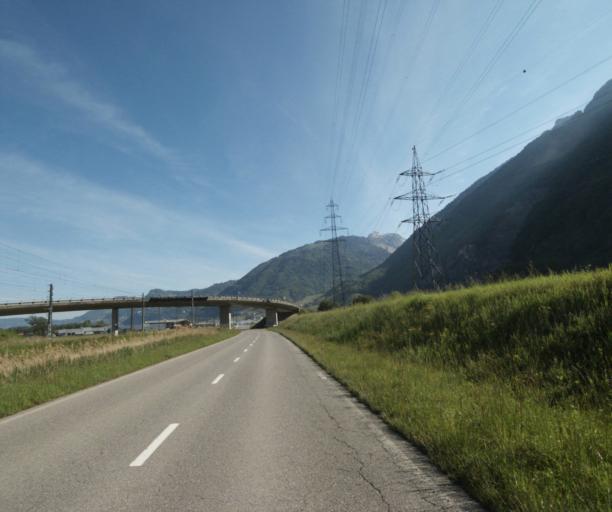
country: CH
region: Vaud
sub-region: Aigle District
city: Villeneuve
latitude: 46.3771
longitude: 6.9278
